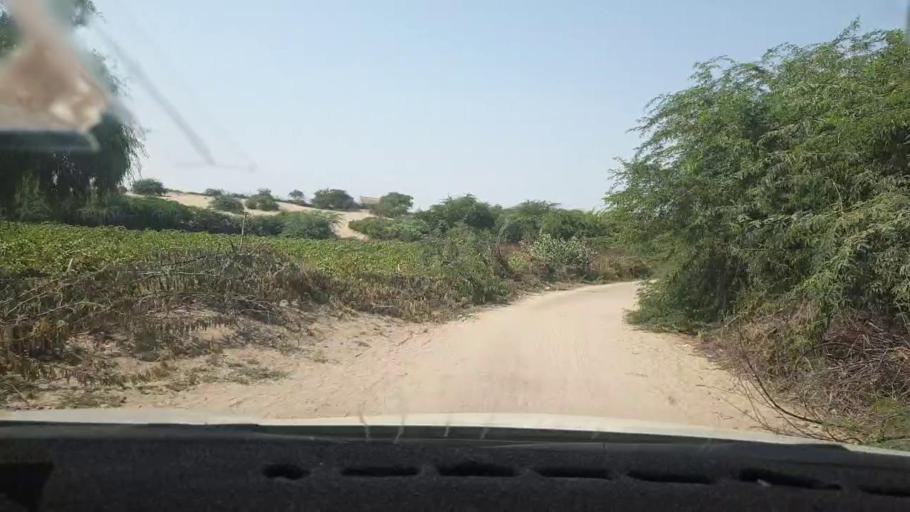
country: PK
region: Sindh
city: Tando Mittha Khan
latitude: 25.8768
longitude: 69.3872
